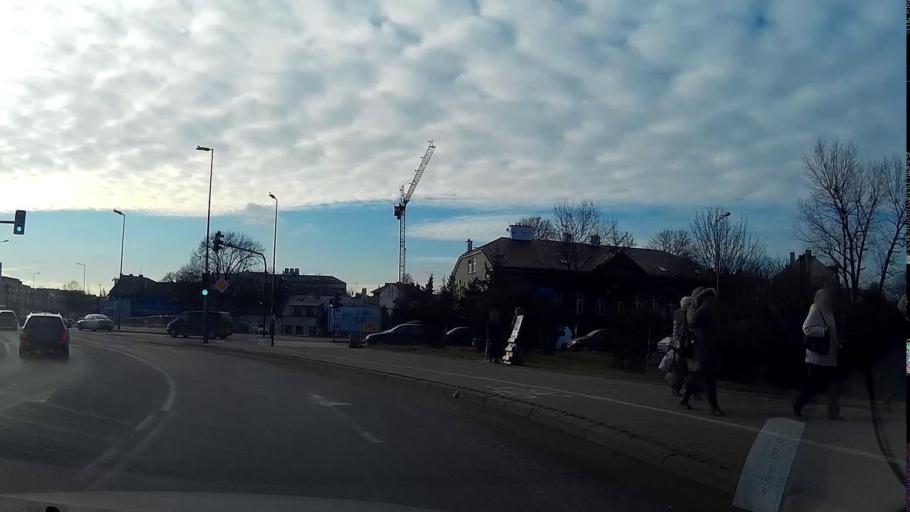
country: PL
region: Lesser Poland Voivodeship
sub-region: Krakow
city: Krakow
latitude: 50.0492
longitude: 19.9319
